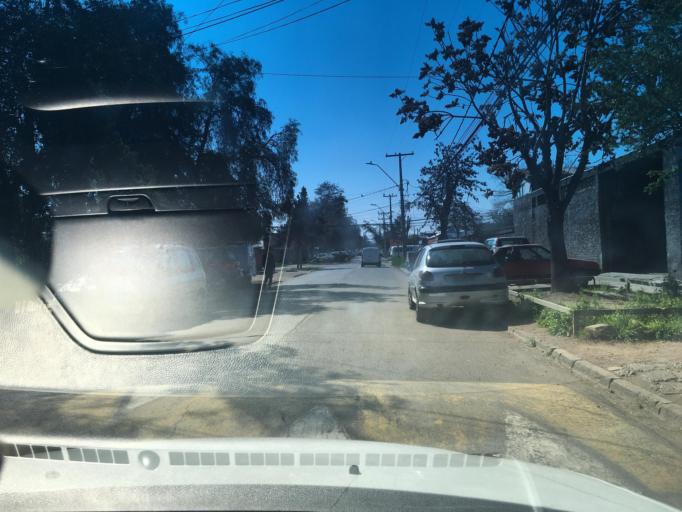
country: CL
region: Santiago Metropolitan
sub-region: Provincia de Santiago
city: Villa Presidente Frei, Nunoa, Santiago, Chile
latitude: -33.4669
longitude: -70.5693
